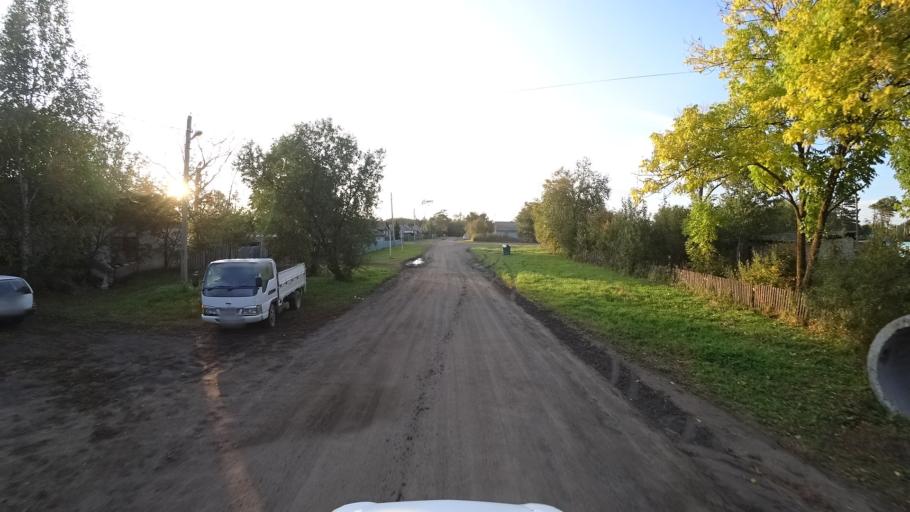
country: RU
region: Amur
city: Arkhara
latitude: 49.3604
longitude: 130.1155
